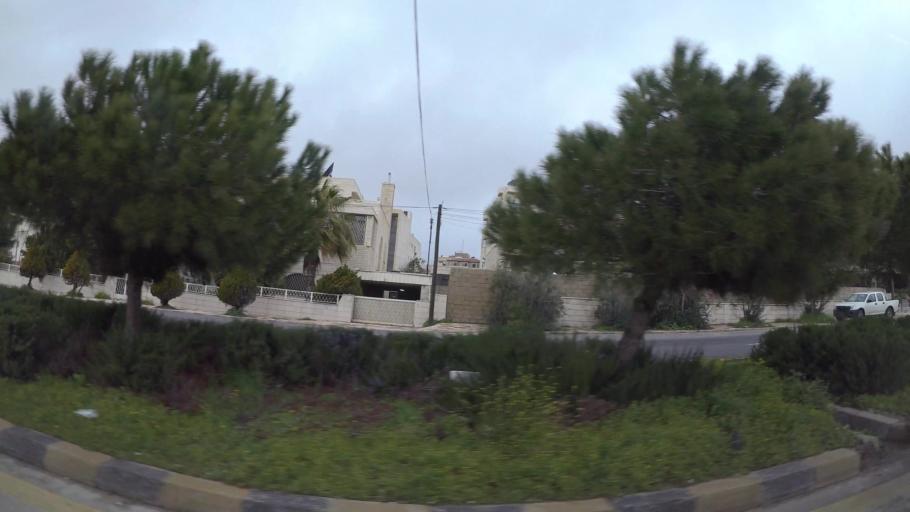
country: JO
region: Amman
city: Wadi as Sir
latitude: 31.9469
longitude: 35.8745
